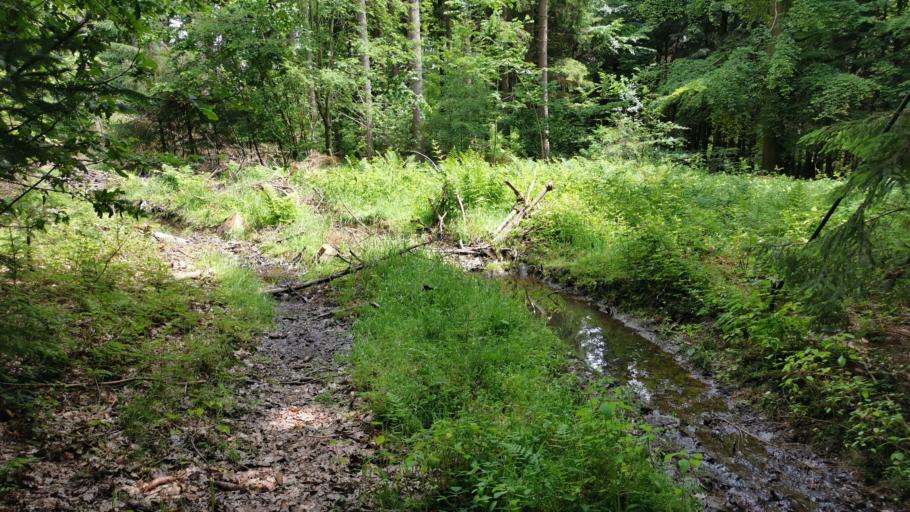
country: DE
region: Bavaria
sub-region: Upper Bavaria
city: Baierbrunn
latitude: 48.0106
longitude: 11.4686
